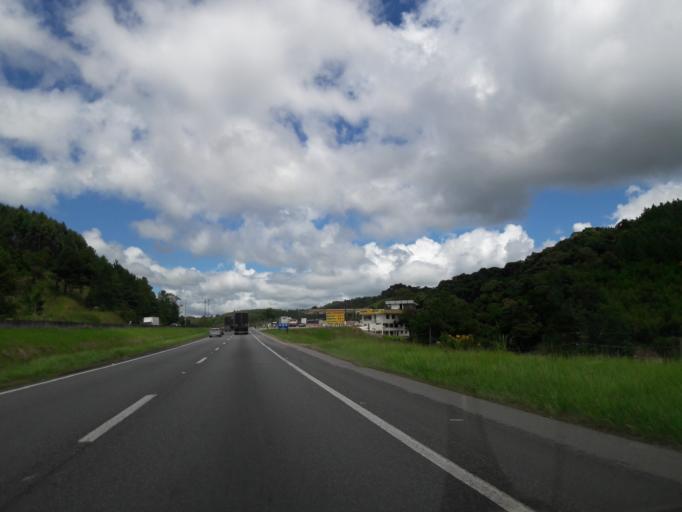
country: BR
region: Parana
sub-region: Campina Grande Do Sul
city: Campina Grande do Sul
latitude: -25.1189
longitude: -48.8547
